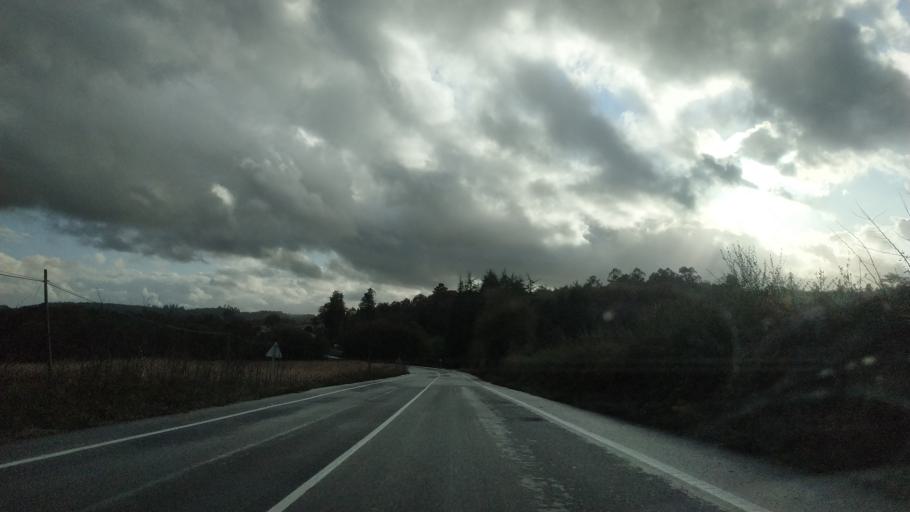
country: ES
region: Galicia
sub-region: Provincia da Coruna
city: Arzua
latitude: 42.9555
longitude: -8.1568
